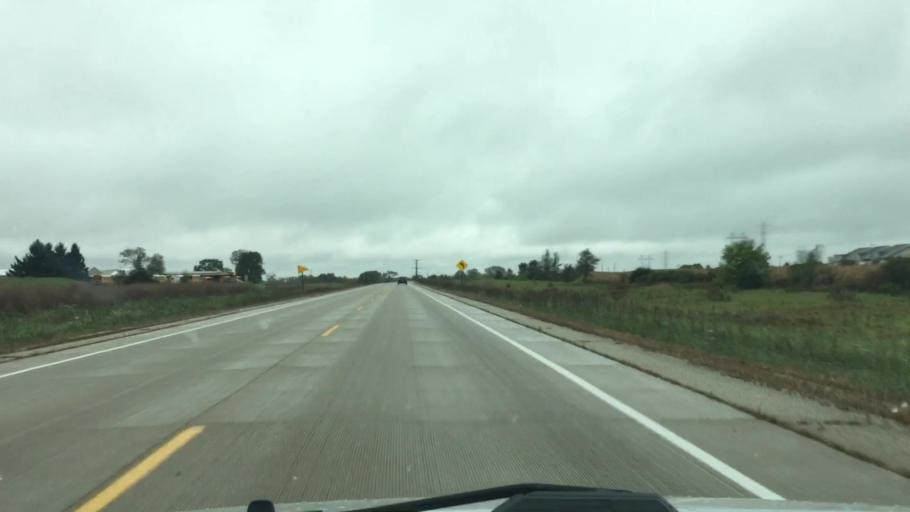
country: US
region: Wisconsin
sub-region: Walworth County
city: Whitewater
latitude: 42.8192
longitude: -88.7197
